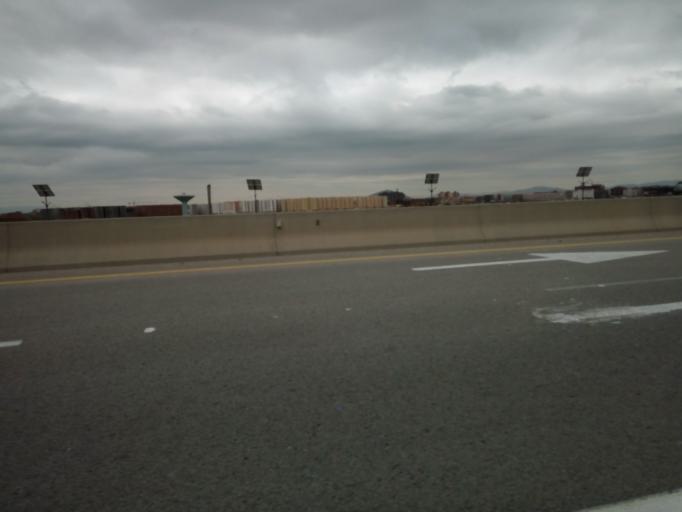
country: DZ
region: Setif
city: El Eulma
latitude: 36.1766
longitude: 5.6791
